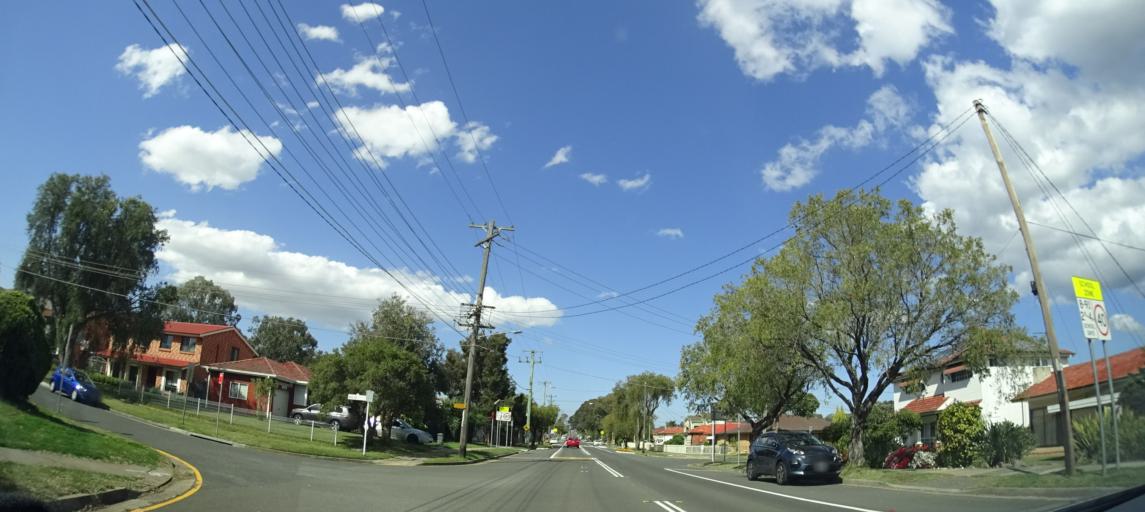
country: AU
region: New South Wales
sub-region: Bankstown
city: Milperra
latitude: -33.9457
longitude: 150.9981
